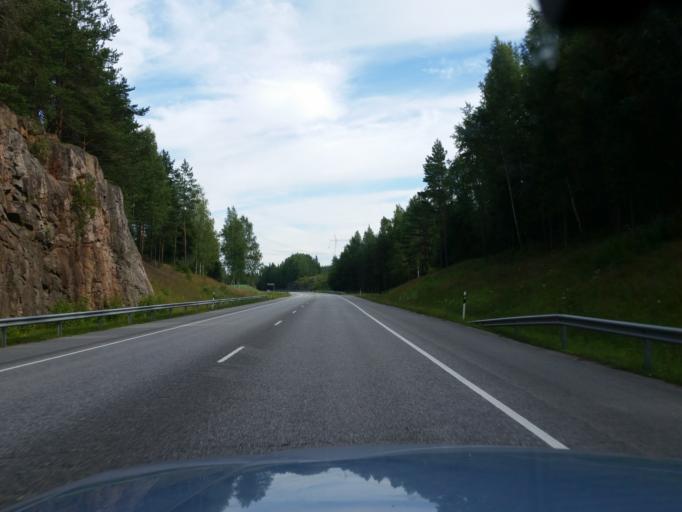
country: FI
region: Uusimaa
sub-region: Raaseporin
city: Karis
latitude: 60.0712
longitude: 23.7783
